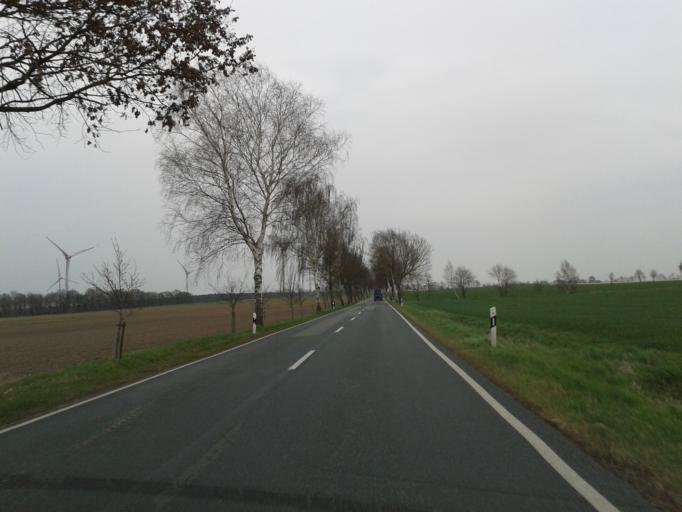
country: DE
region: Lower Saxony
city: Woltersdorf
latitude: 52.9126
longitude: 11.2911
